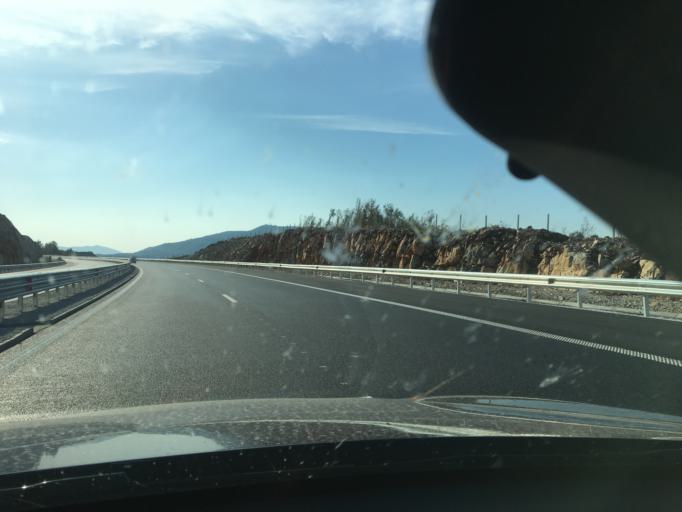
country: BG
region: Lovech
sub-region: Obshtina Yablanitsa
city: Yablanitsa
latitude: 43.0469
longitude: 24.1324
